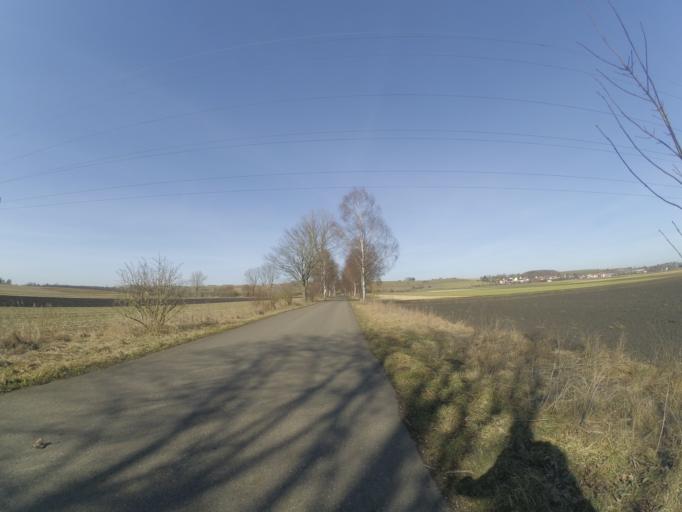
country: DE
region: Baden-Wuerttemberg
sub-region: Tuebingen Region
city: Rammingen
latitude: 48.5046
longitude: 10.1879
